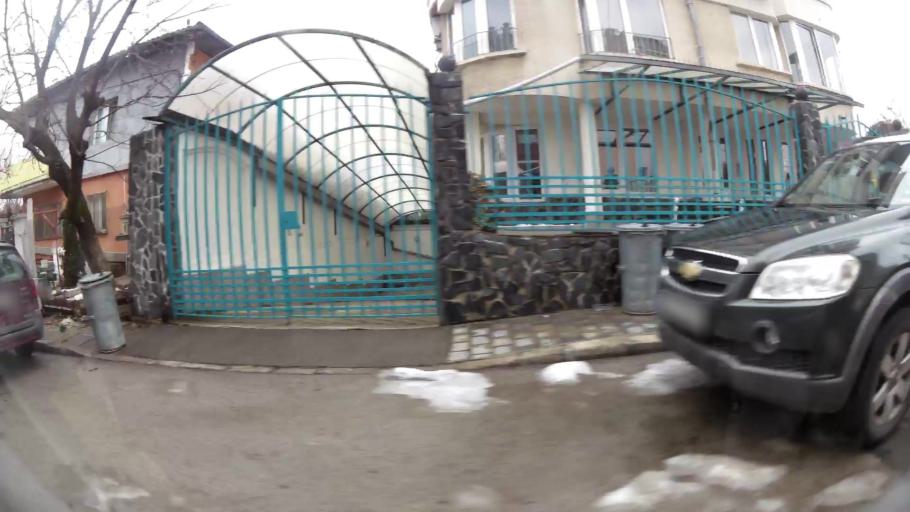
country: BG
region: Sofiya
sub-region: Obshtina Bozhurishte
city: Bozhurishte
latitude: 42.6715
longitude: 23.2397
